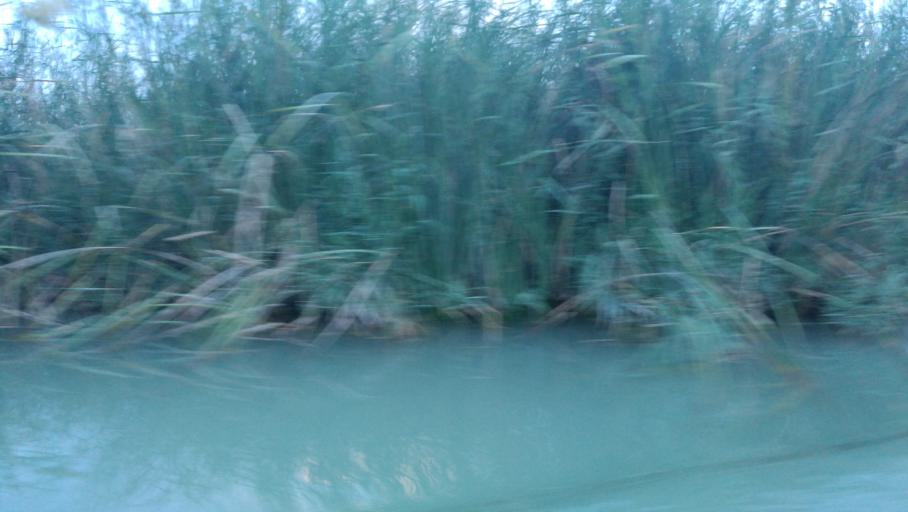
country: IQ
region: Dhi Qar
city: Al Jabayish
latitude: 30.9774
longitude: 47.0404
